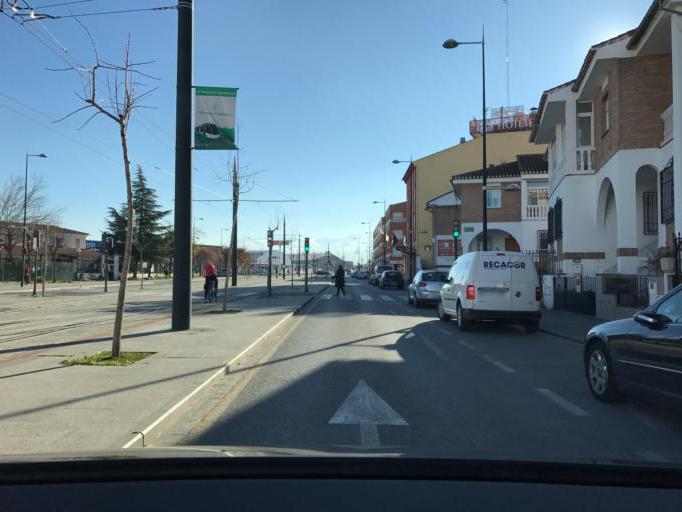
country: ES
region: Andalusia
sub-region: Provincia de Granada
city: Albolote
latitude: 37.2276
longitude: -3.6524
